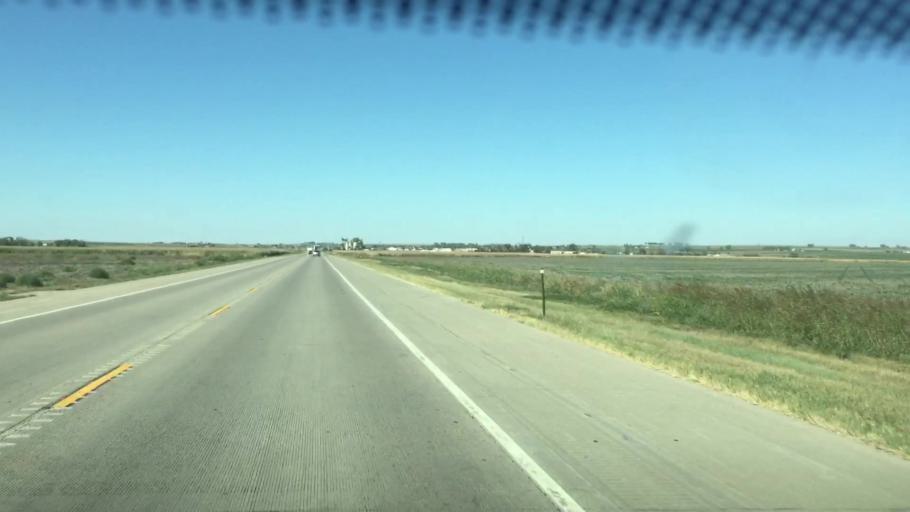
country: US
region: Colorado
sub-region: Prowers County
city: Lamar
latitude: 38.1305
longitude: -102.7237
